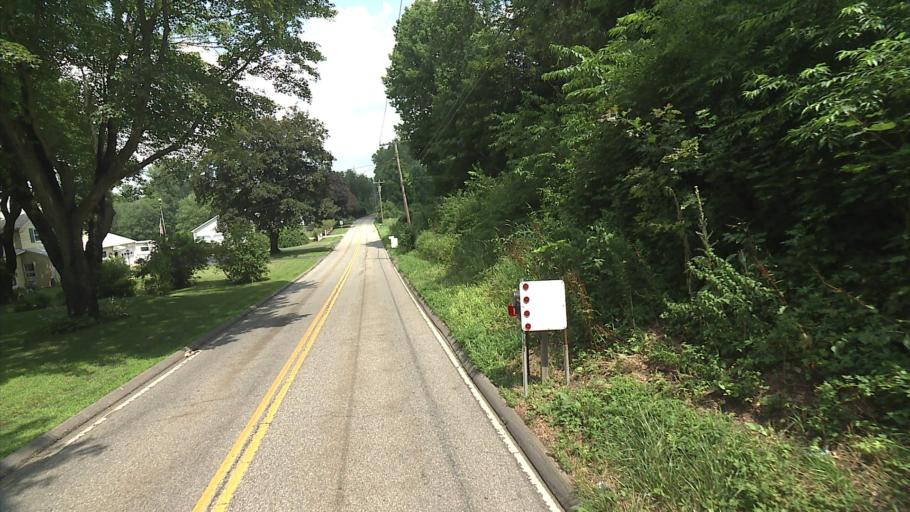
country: US
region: Connecticut
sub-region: New London County
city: Baltic
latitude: 41.6099
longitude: -72.1250
